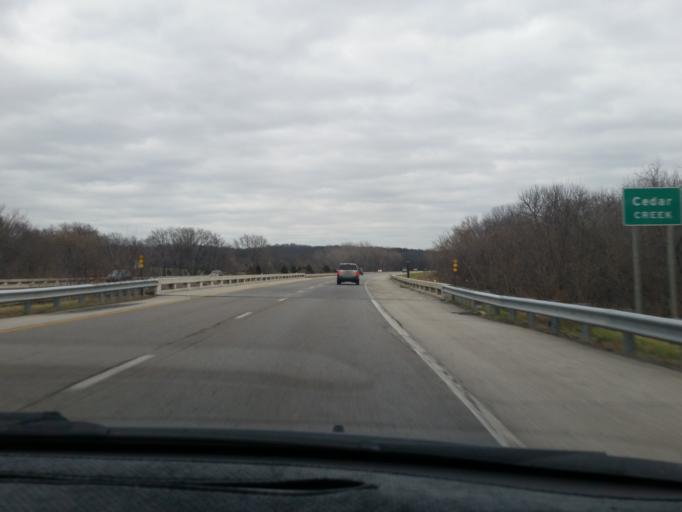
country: US
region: Kansas
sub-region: Johnson County
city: De Soto
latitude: 38.9565
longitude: -94.9165
